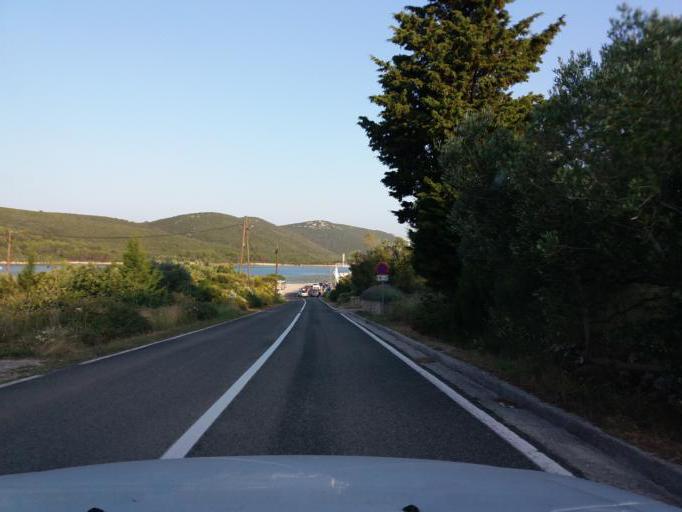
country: HR
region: Zadarska
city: Ugljan
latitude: 44.0836
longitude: 14.9994
